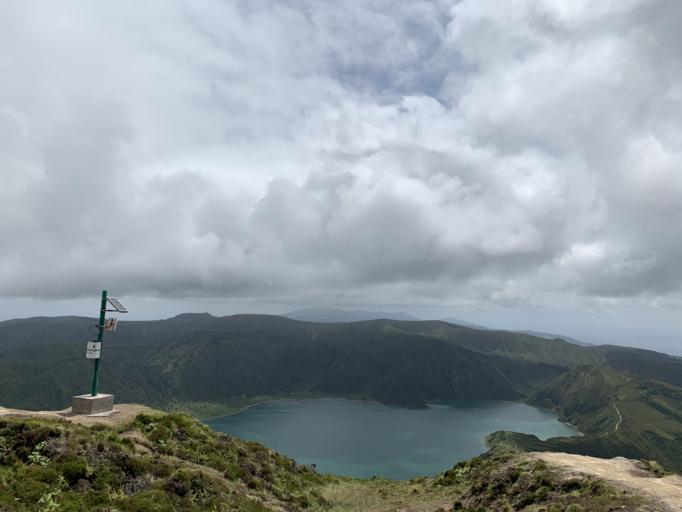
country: PT
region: Azores
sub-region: Vila Franca do Campo
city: Vila Franca do Campo
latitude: 37.7604
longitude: -25.4912
